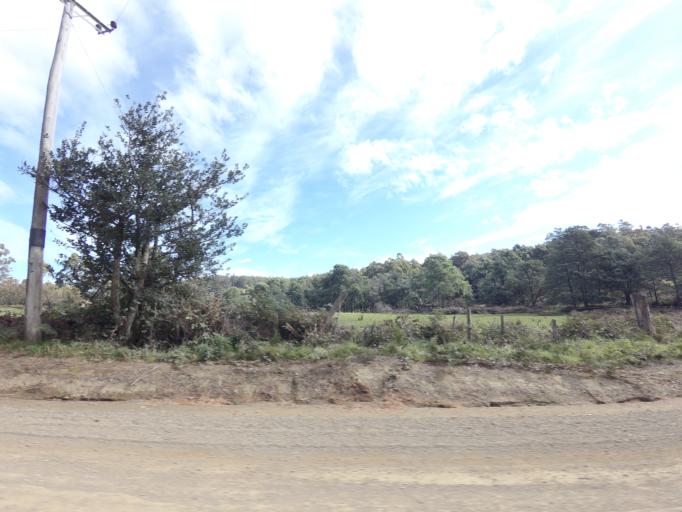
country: AU
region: Tasmania
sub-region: Clarence
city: Sandford
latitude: -43.1454
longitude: 147.7640
